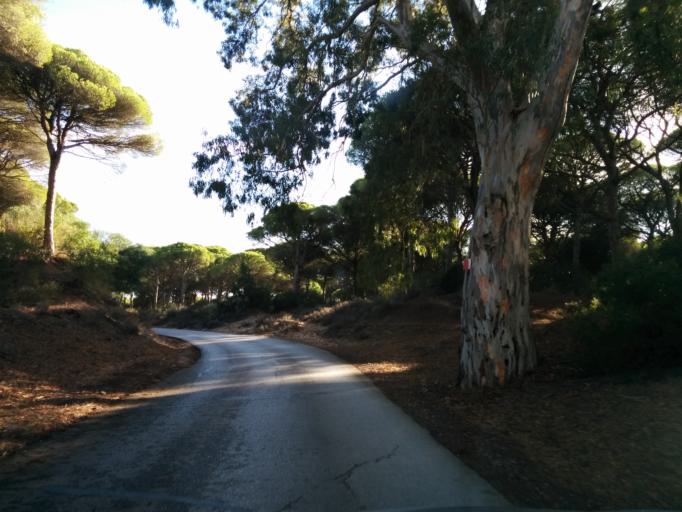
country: ES
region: Andalusia
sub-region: Provincia de Cadiz
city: Vejer de la Frontera
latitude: 36.2038
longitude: -5.9802
